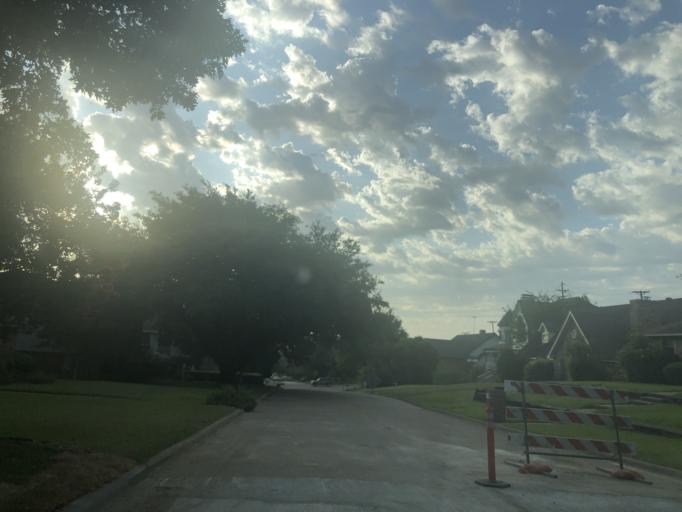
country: US
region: Texas
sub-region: Dallas County
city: Grand Prairie
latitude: 32.7606
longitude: -97.0212
